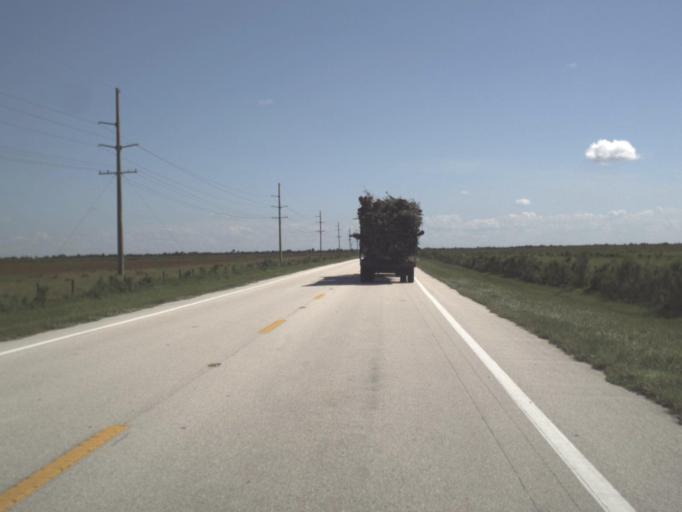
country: US
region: Florida
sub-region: Glades County
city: Moore Haven
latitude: 26.8123
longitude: -81.2357
